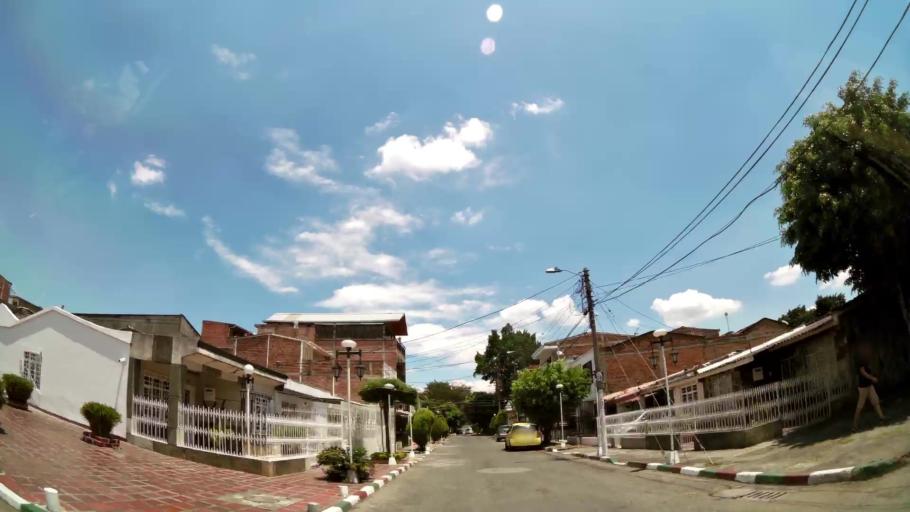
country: CO
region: Valle del Cauca
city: Cali
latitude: 3.4517
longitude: -76.4994
